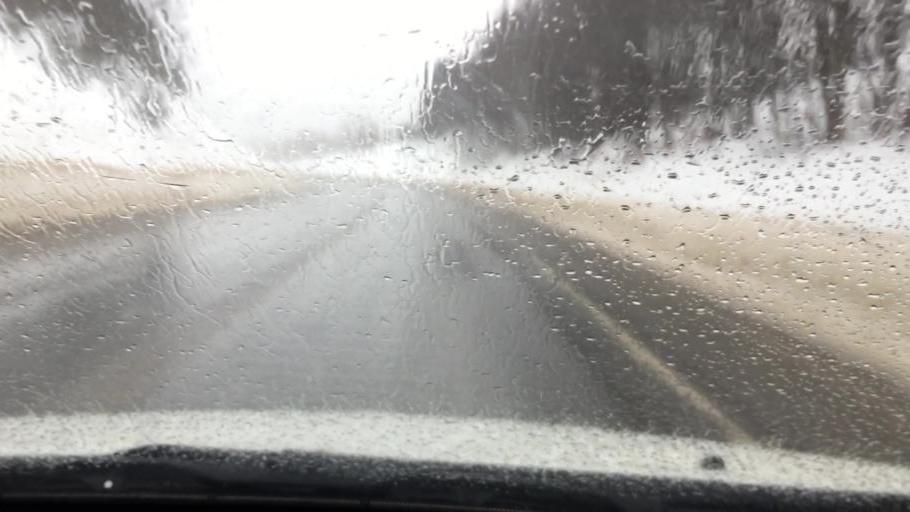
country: US
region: Michigan
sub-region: Antrim County
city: Mancelona
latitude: 44.9541
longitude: -85.0518
